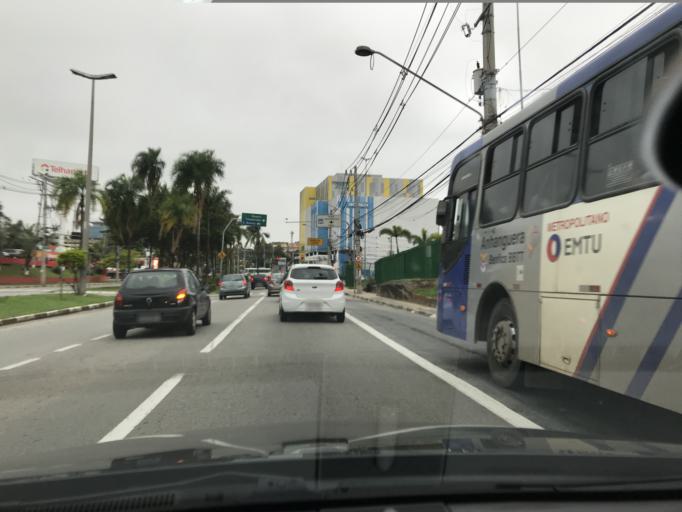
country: BR
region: Sao Paulo
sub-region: Carapicuiba
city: Carapicuiba
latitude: -23.5026
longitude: -46.8336
